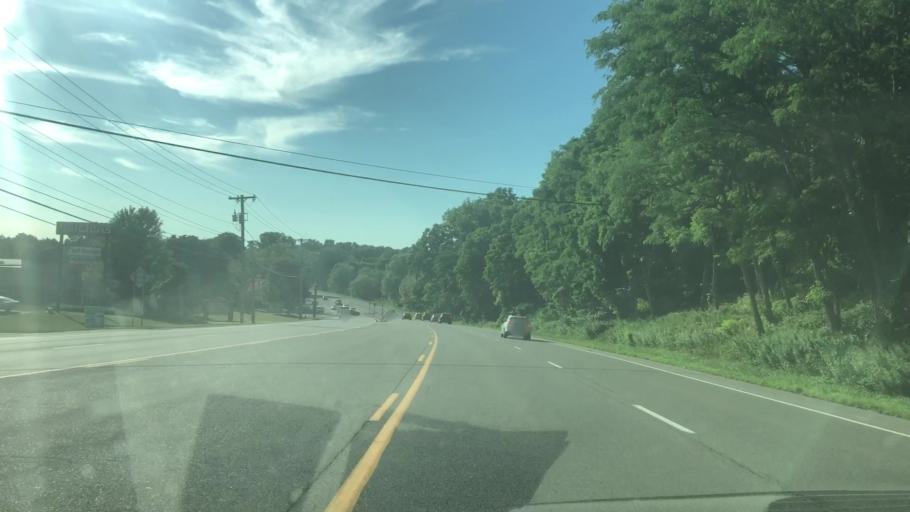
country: US
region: New York
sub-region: Ontario County
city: Victor
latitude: 43.0340
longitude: -77.4437
